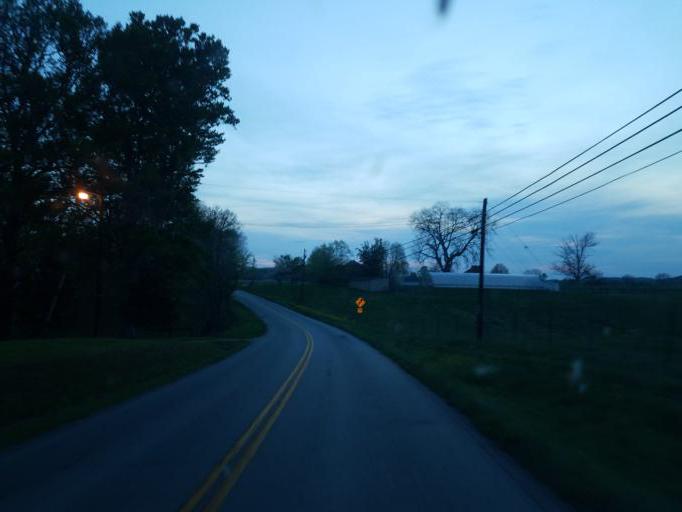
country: US
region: Kentucky
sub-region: Hart County
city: Munfordville
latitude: 37.2718
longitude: -85.8547
